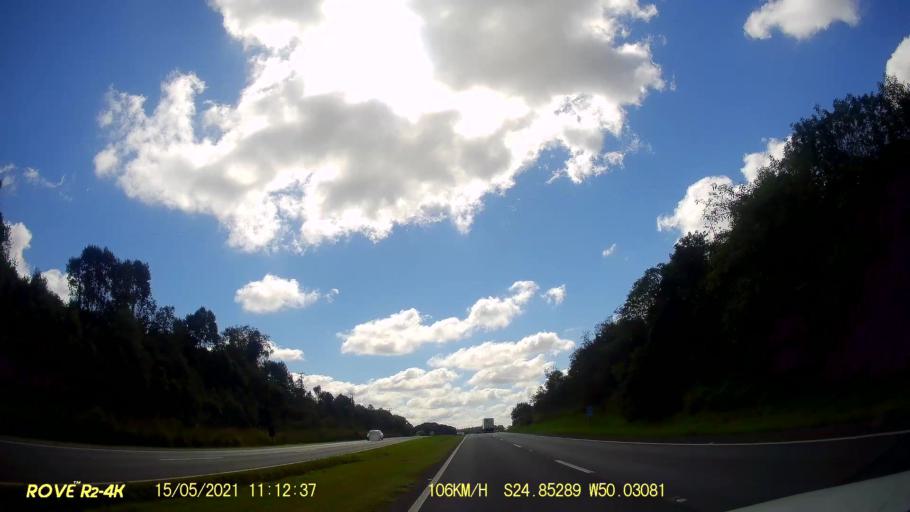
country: BR
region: Parana
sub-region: Castro
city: Castro
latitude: -24.8530
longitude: -50.0308
